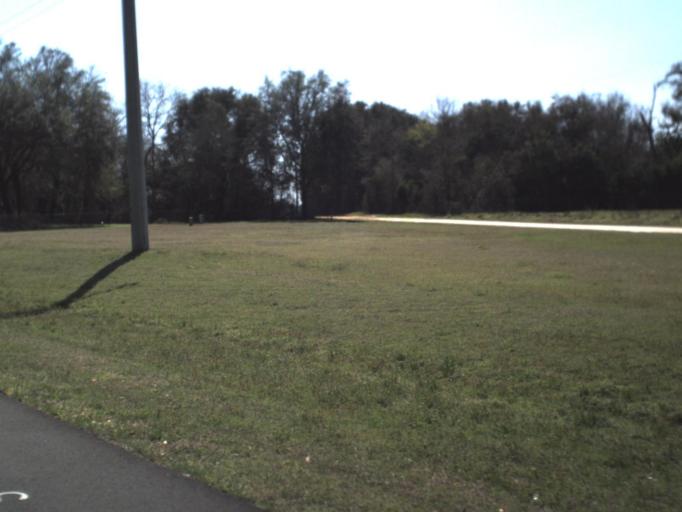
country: US
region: Florida
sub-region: Jackson County
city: Sneads
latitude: 30.8009
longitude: -85.0316
